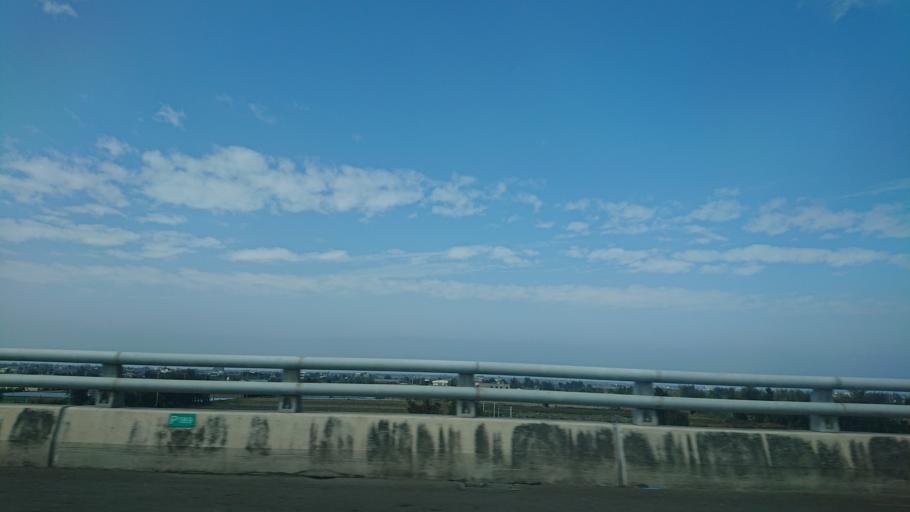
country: TW
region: Taiwan
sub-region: Yunlin
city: Douliu
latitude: 23.8492
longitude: 120.2945
